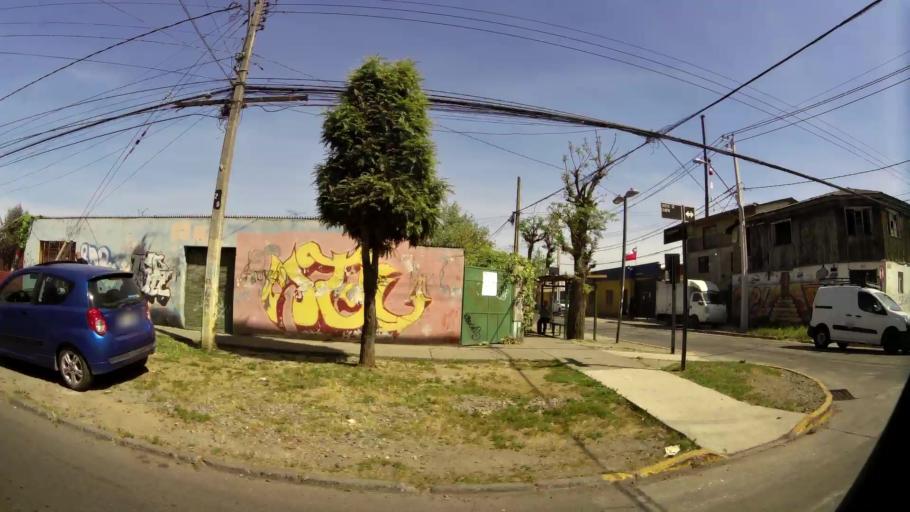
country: CL
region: Santiago Metropolitan
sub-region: Provincia de Maipo
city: San Bernardo
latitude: -33.5294
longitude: -70.6919
